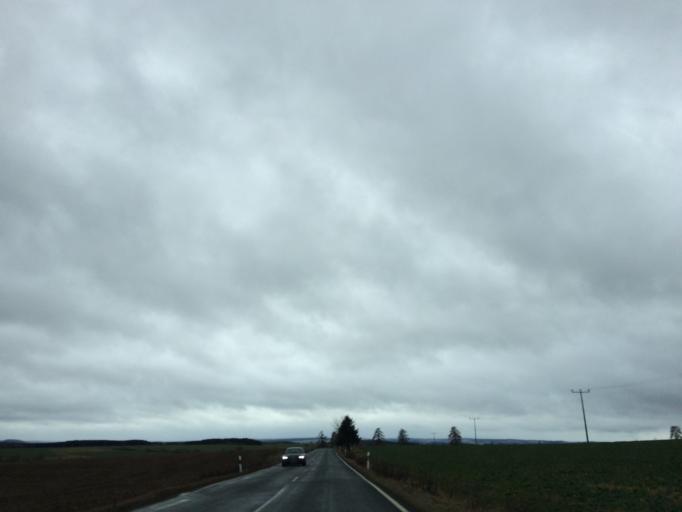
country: DE
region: Thuringia
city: Dreba
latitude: 50.6759
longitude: 11.7509
